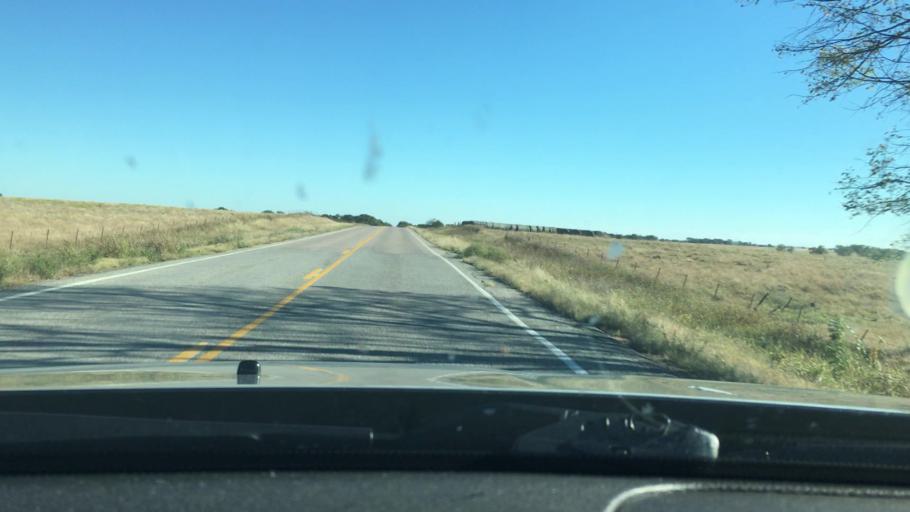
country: US
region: Oklahoma
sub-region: Marshall County
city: Madill
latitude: 34.1215
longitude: -96.7307
